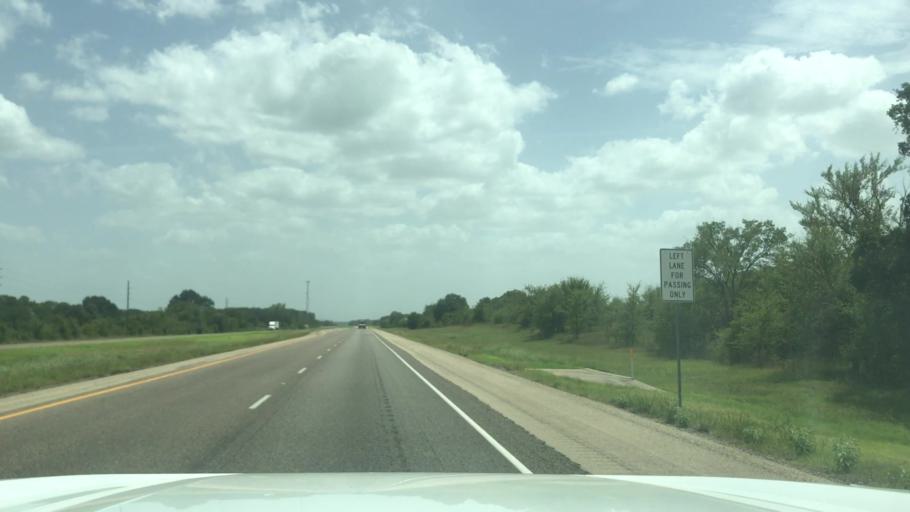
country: US
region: Texas
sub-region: Robertson County
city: Calvert
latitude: 31.0430
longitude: -96.7106
